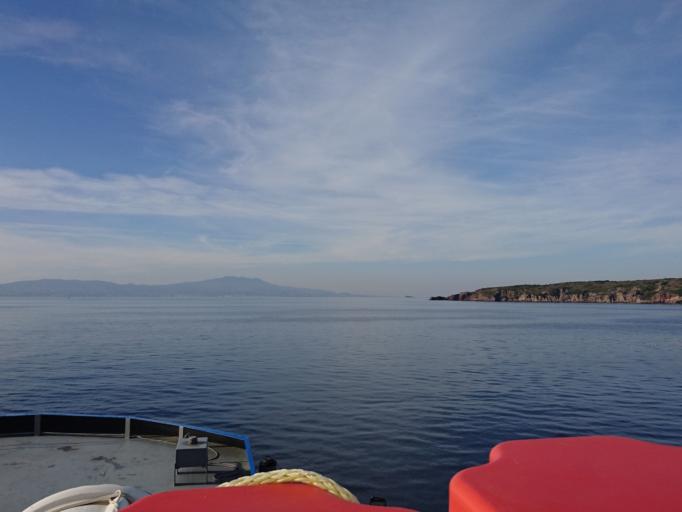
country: TR
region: Mugla
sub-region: Bodrum
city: Bodrum
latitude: 36.9961
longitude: 27.3982
